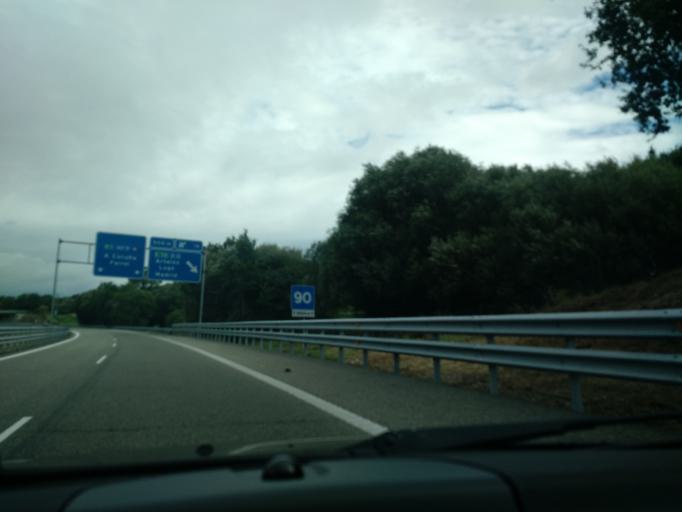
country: ES
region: Galicia
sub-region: Provincia da Coruna
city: Betanzos
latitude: 43.2674
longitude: -8.2527
